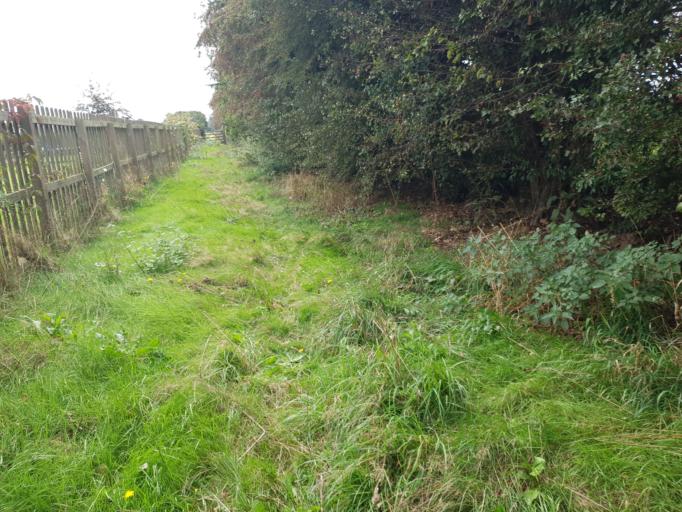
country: GB
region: England
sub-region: Suffolk
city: East Bergholt
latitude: 51.9327
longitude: 0.9917
